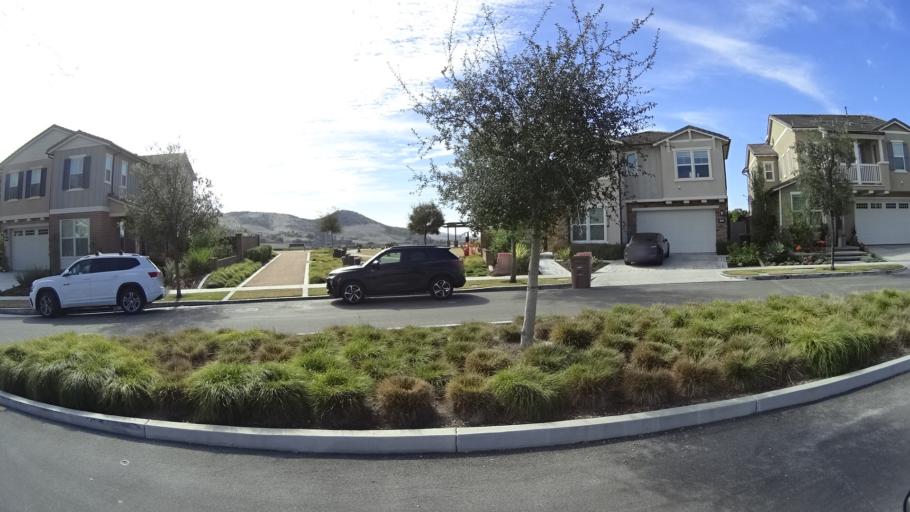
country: US
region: California
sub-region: Orange County
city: Ladera Ranch
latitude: 33.5302
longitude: -117.6044
